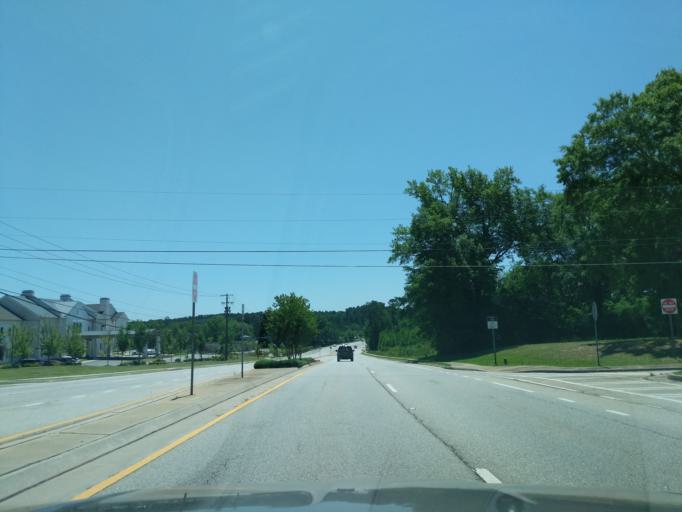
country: US
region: Georgia
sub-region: Columbia County
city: Martinez
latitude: 33.5427
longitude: -82.0842
